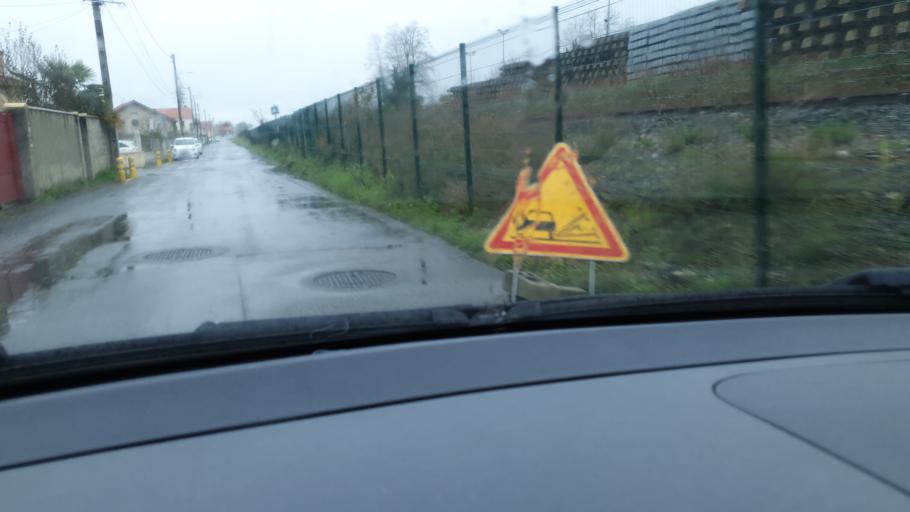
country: FR
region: Midi-Pyrenees
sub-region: Departement des Hautes-Pyrenees
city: Tarbes
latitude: 43.2487
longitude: 0.0533
